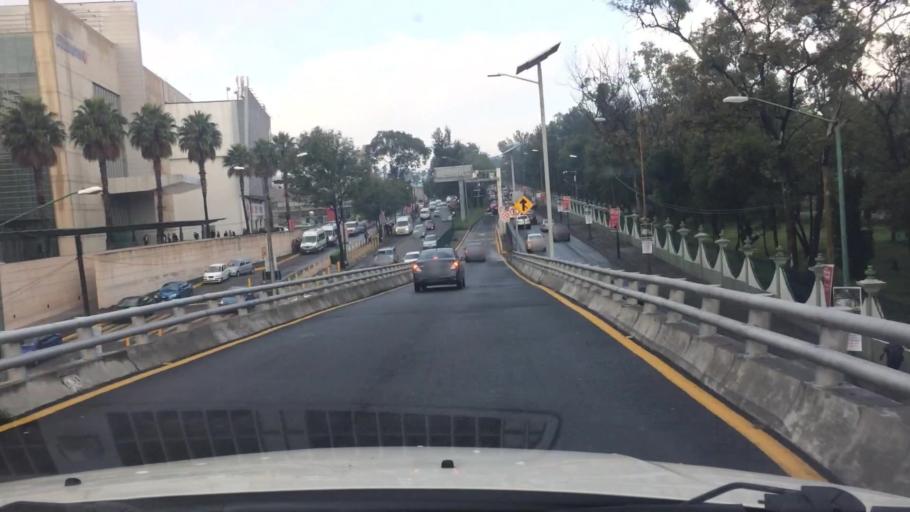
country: MX
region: Mexico City
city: Miguel Hidalgo
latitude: 19.4425
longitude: -99.2224
